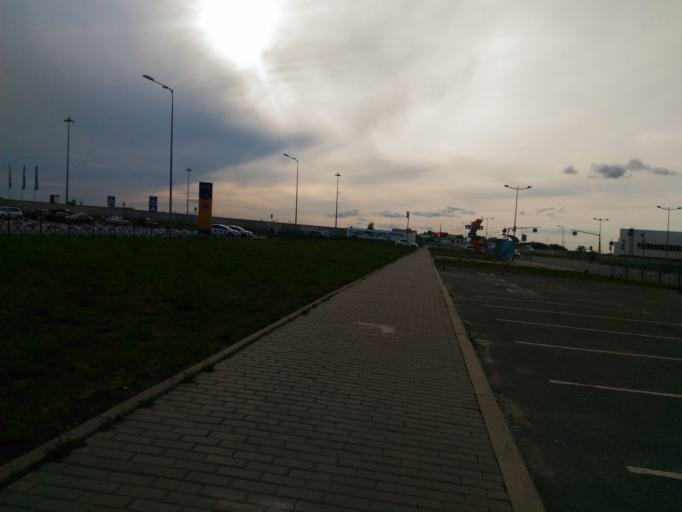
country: RU
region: Ulyanovsk
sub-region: Ulyanovskiy Rayon
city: Ulyanovsk
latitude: 54.2873
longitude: 48.2785
